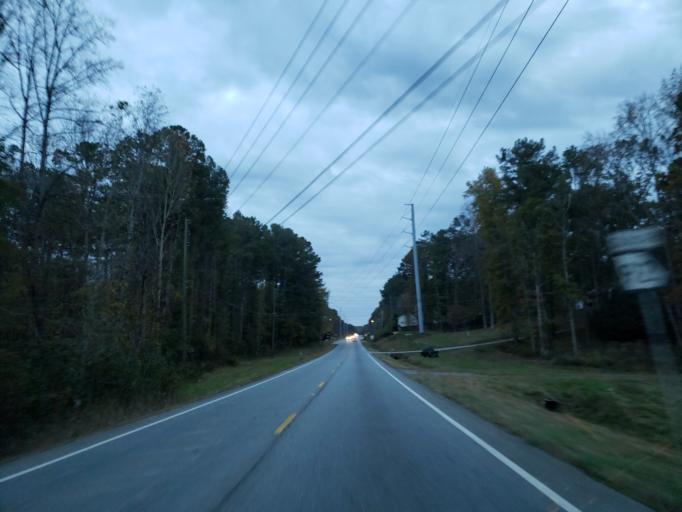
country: US
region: Georgia
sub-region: Paulding County
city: Hiram
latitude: 33.9680
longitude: -84.7397
